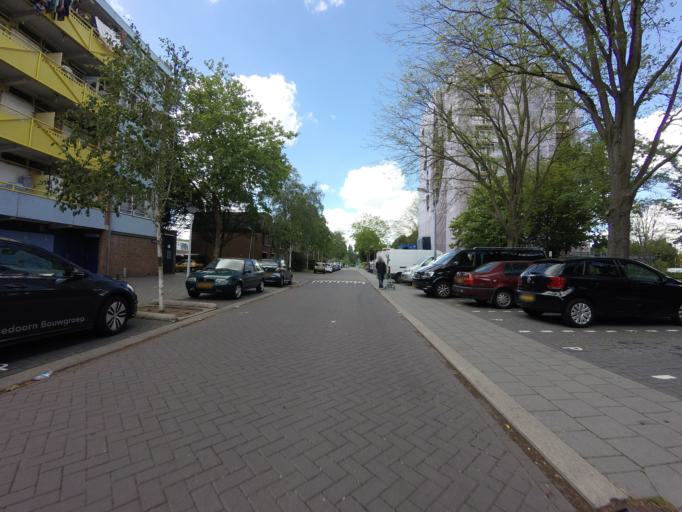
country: NL
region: North Holland
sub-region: Gemeente Zaanstad
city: Zaandam
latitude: 52.4378
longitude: 4.8522
